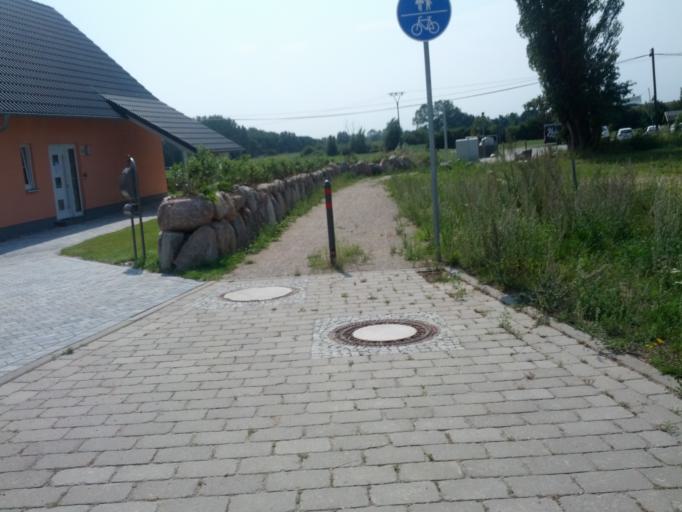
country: DE
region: Mecklenburg-Vorpommern
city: Bastorf
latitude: 54.1006
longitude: 11.6251
